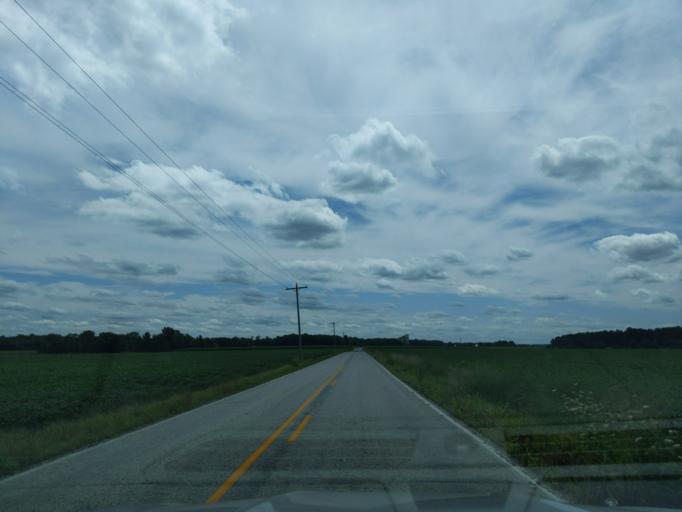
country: US
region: Indiana
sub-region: Ripley County
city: Batesville
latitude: 39.2321
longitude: -85.2679
